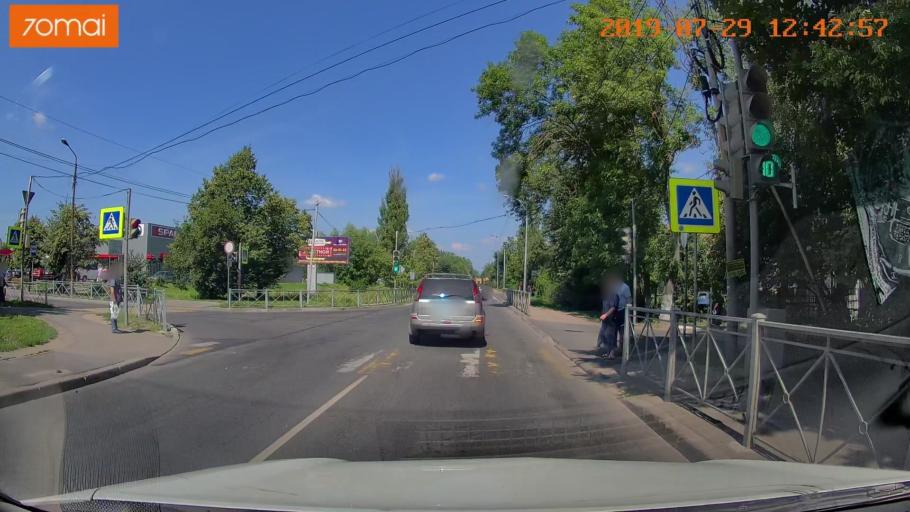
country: RU
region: Kaliningrad
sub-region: Gorod Kaliningrad
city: Kaliningrad
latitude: 54.6738
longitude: 20.5429
